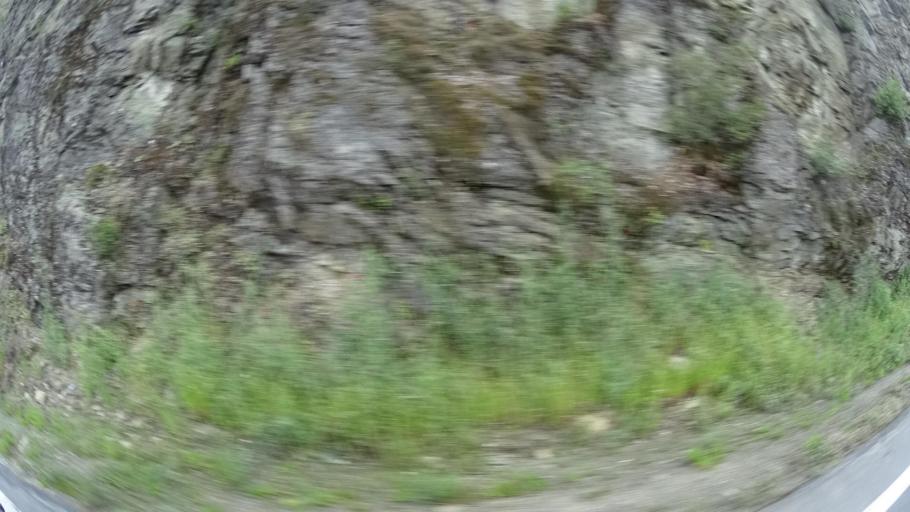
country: US
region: California
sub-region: Humboldt County
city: Willow Creek
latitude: 41.1157
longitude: -123.6883
